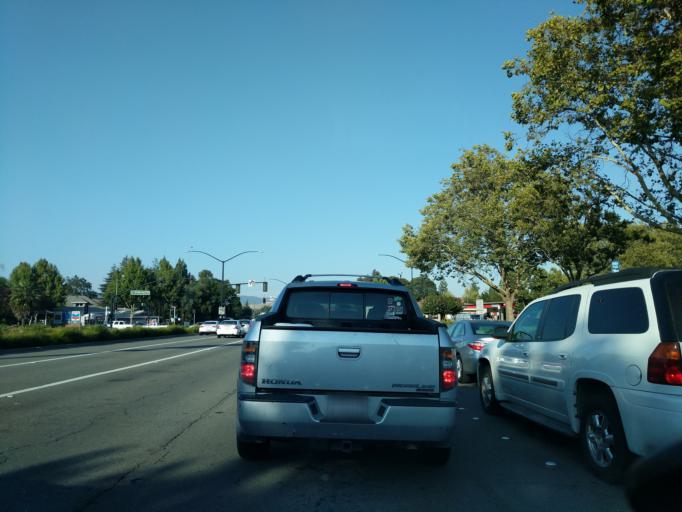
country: US
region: California
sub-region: Contra Costa County
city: San Ramon
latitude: 37.7754
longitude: -121.9792
